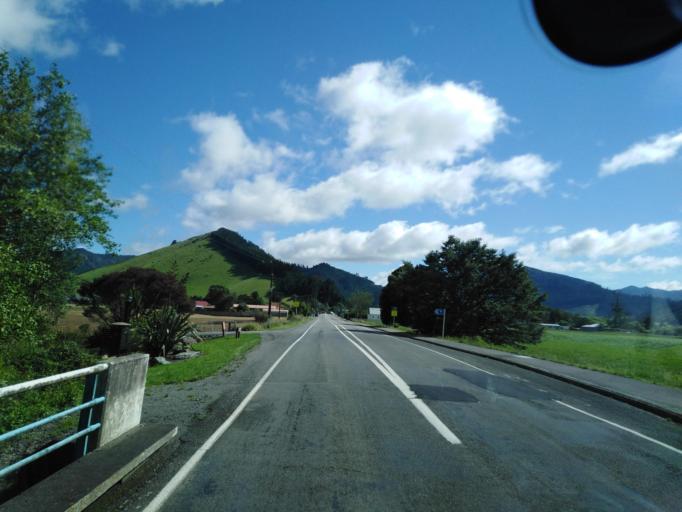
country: NZ
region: Nelson
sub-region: Nelson City
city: Nelson
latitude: -41.2324
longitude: 173.5816
